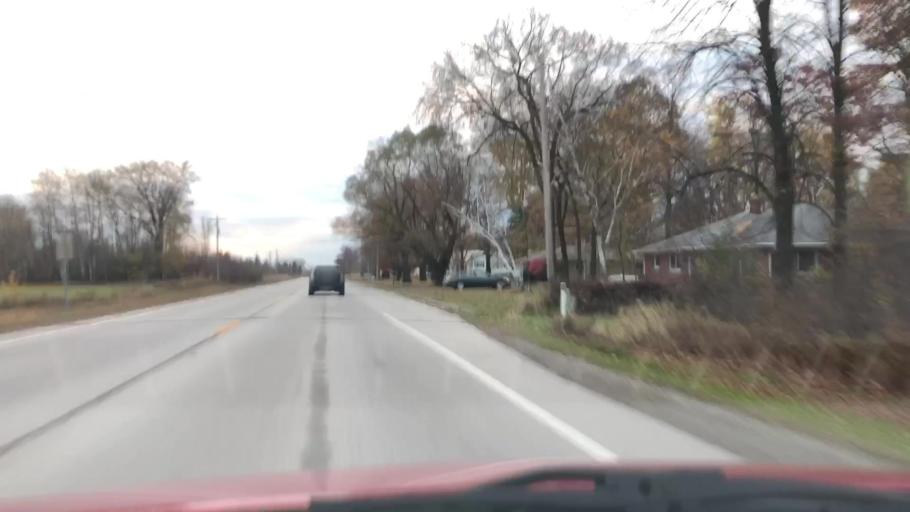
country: US
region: Wisconsin
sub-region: Brown County
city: Oneida
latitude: 44.4442
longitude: -88.1869
